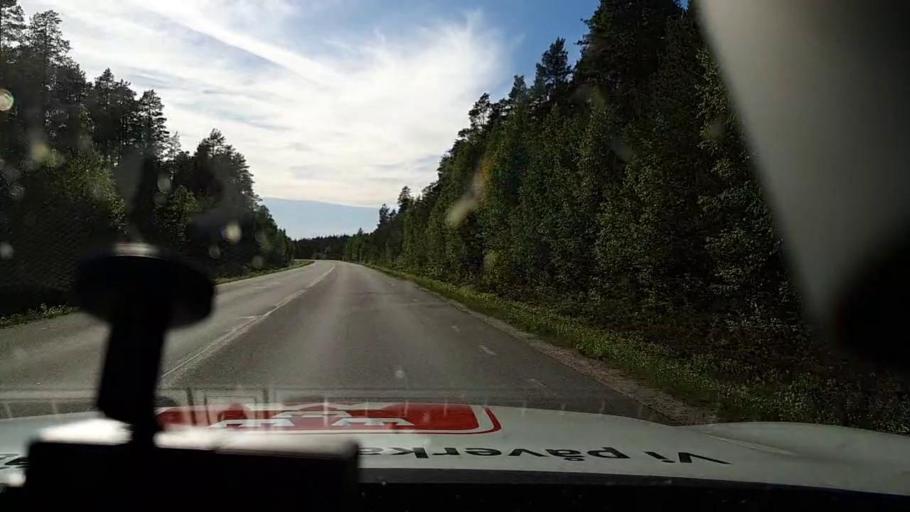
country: SE
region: Norrbotten
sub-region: Lulea Kommun
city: Gammelstad
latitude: 65.6629
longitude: 22.0865
